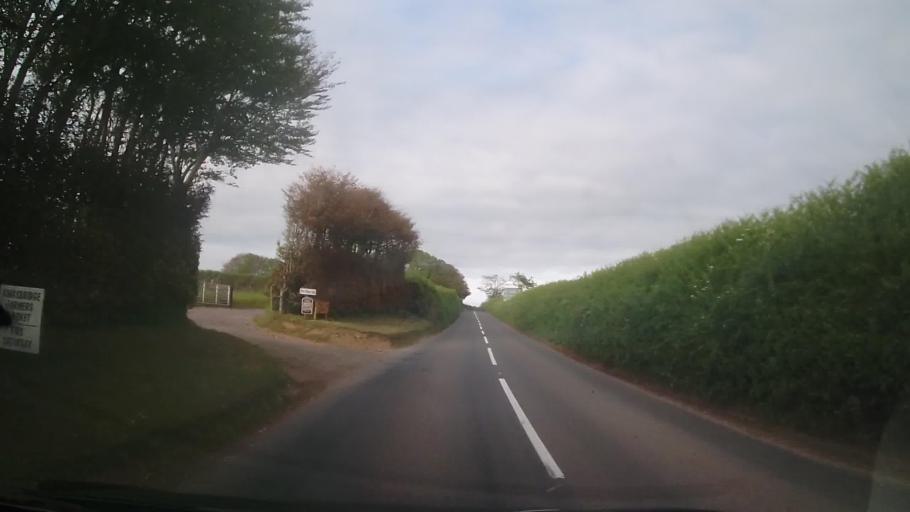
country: GB
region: England
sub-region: Devon
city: Kingsbridge
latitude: 50.2975
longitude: -3.8181
